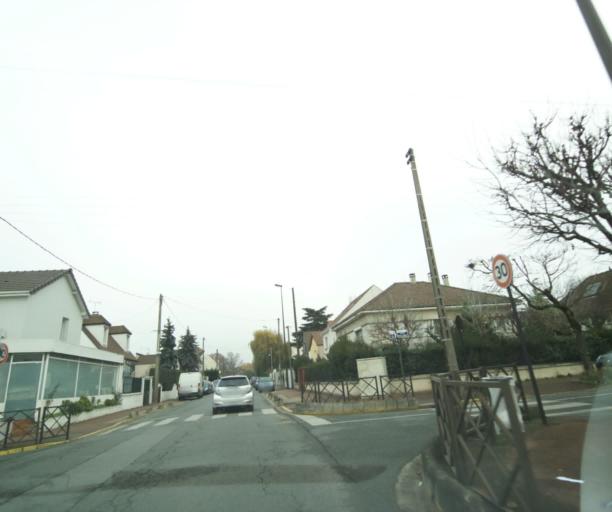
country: FR
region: Ile-de-France
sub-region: Departement de Seine-Saint-Denis
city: Livry-Gargan
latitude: 48.9189
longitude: 2.5244
